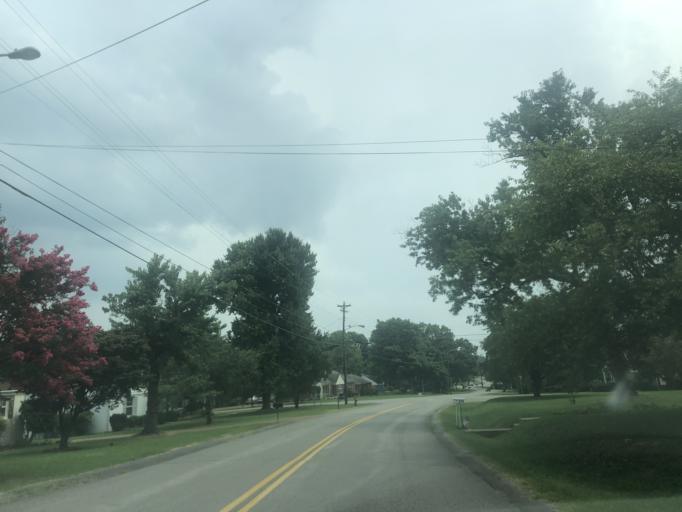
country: US
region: Tennessee
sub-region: Davidson County
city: Lakewood
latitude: 36.1599
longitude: -86.6843
